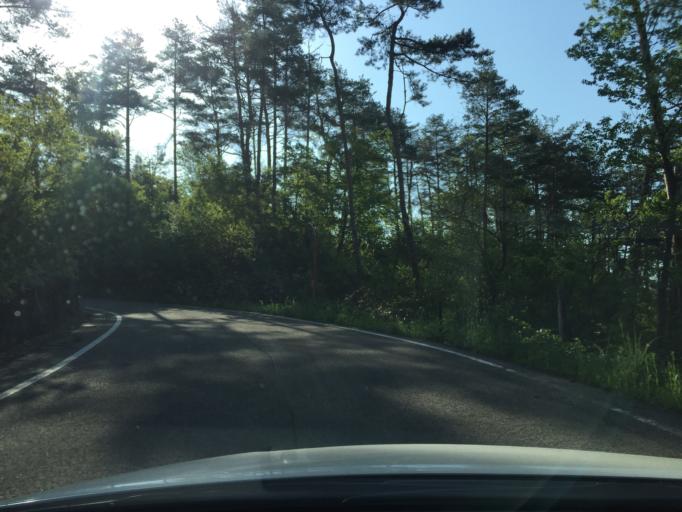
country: JP
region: Fukushima
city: Kitakata
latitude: 37.6719
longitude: 139.8057
